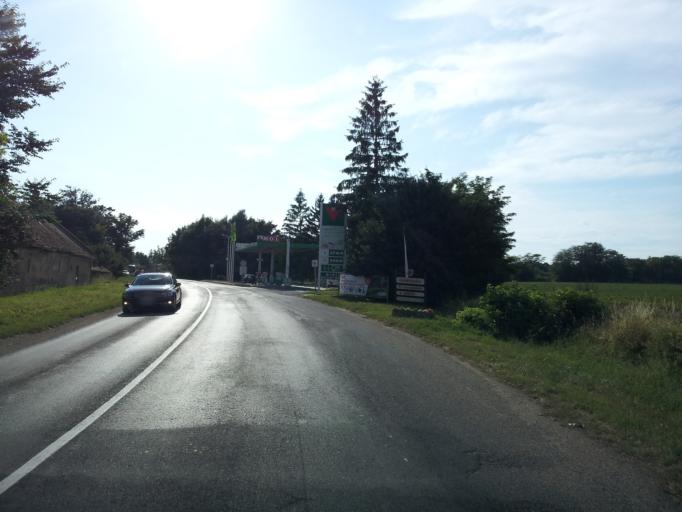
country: HU
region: Veszprem
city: Urkut
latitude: 46.9888
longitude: 17.7055
